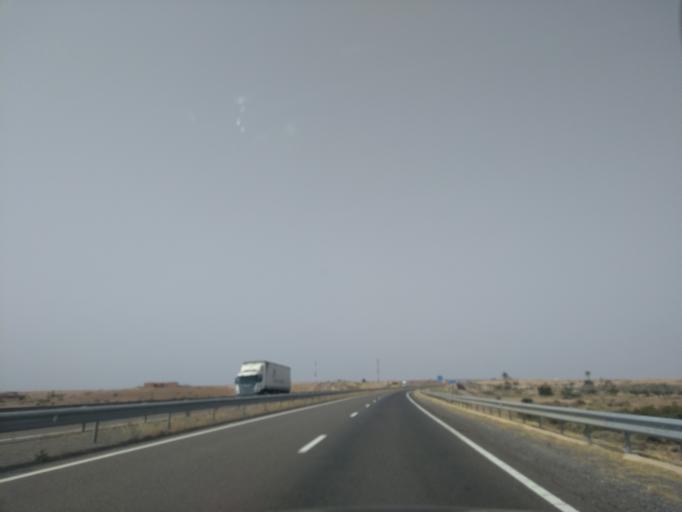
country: MA
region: Marrakech-Tensift-Al Haouz
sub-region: Marrakech
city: Marrakesh
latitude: 31.7279
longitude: -8.2212
